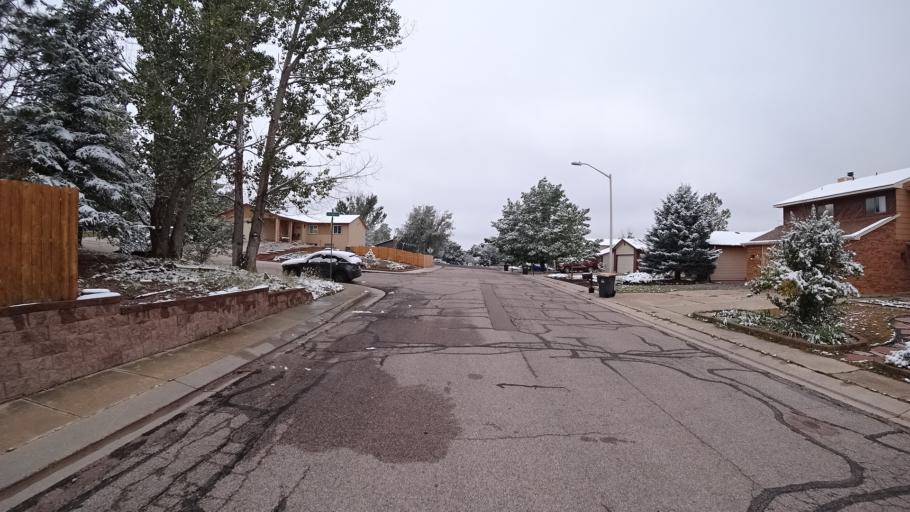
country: US
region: Colorado
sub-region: El Paso County
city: Cimarron Hills
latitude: 38.9235
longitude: -104.7663
